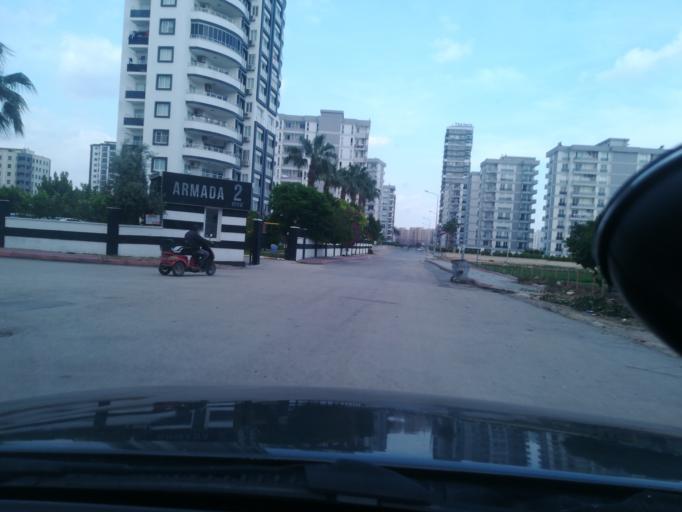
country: TR
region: Adana
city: Seyhan
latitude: 37.0113
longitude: 35.2674
